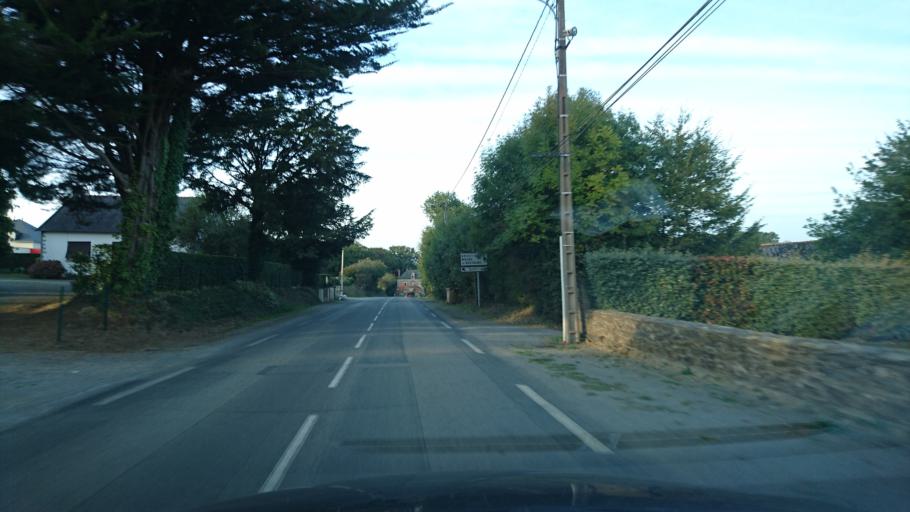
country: FR
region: Brittany
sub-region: Departement d'Ille-et-Vilaine
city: Bains-sur-Oust
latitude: 47.7368
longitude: -2.0498
